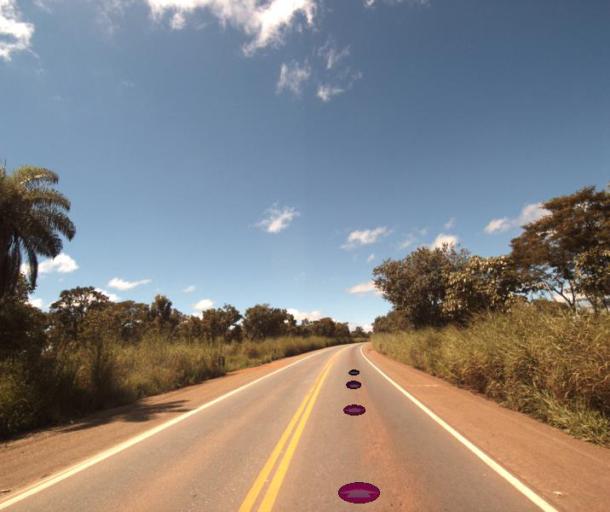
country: BR
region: Goias
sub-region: Jaragua
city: Jaragua
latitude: -15.6810
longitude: -49.3420
